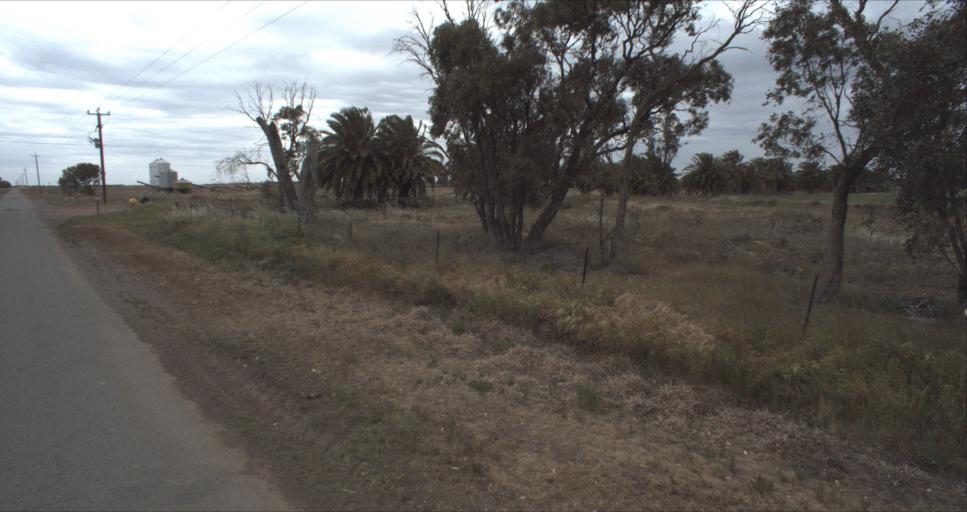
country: AU
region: New South Wales
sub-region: Leeton
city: Leeton
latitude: -34.4201
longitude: 146.3387
